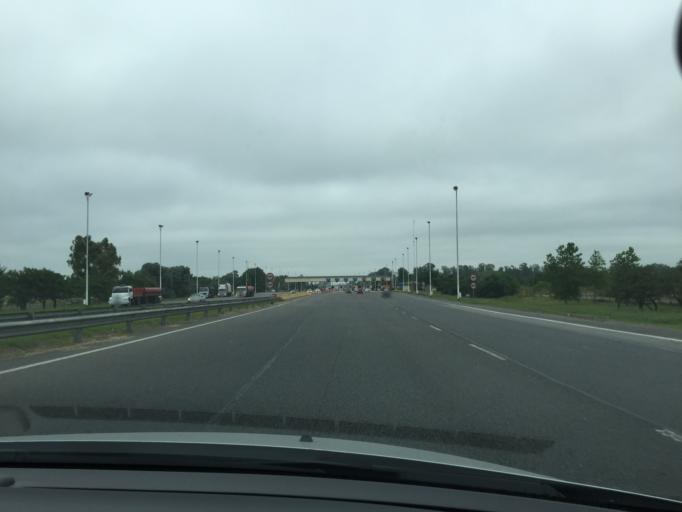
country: AR
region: Buenos Aires
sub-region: Partido de Ezeiza
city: Ezeiza
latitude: -34.8524
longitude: -58.5482
